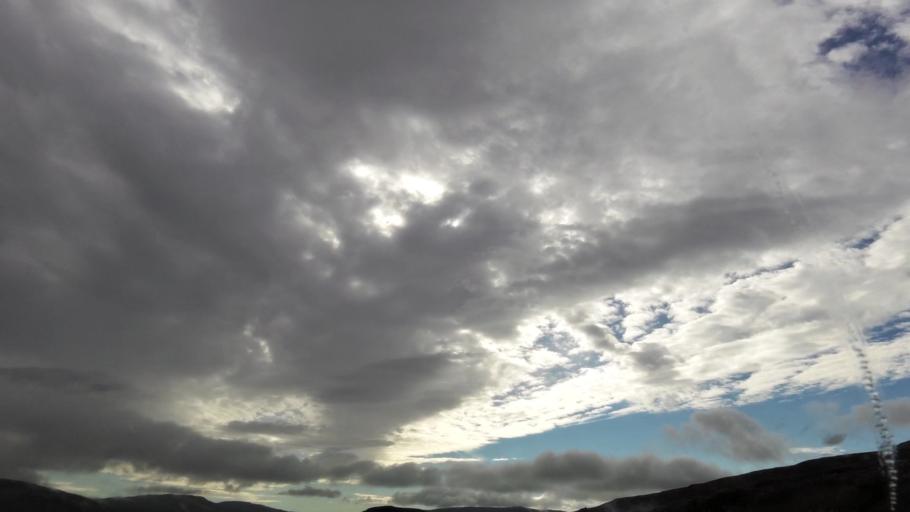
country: IS
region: West
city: Olafsvik
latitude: 65.5382
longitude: -23.8083
